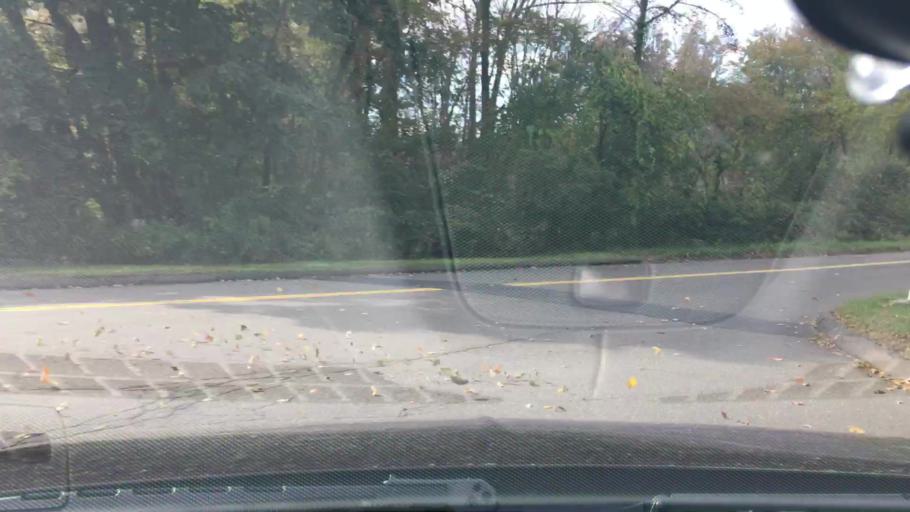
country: US
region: Connecticut
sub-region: New Haven County
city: Meriden
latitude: 41.4904
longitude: -72.7604
